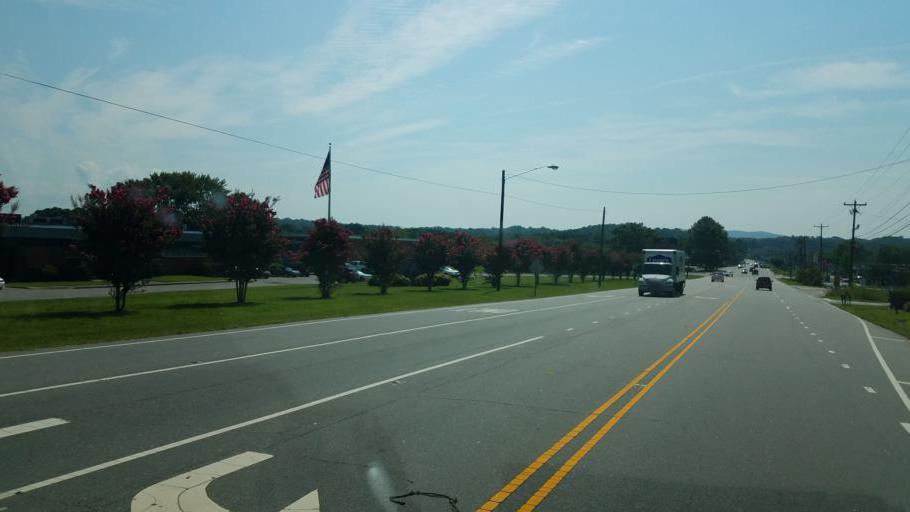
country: US
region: North Carolina
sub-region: Burke County
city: Morganton
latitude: 35.7546
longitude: -81.7191
